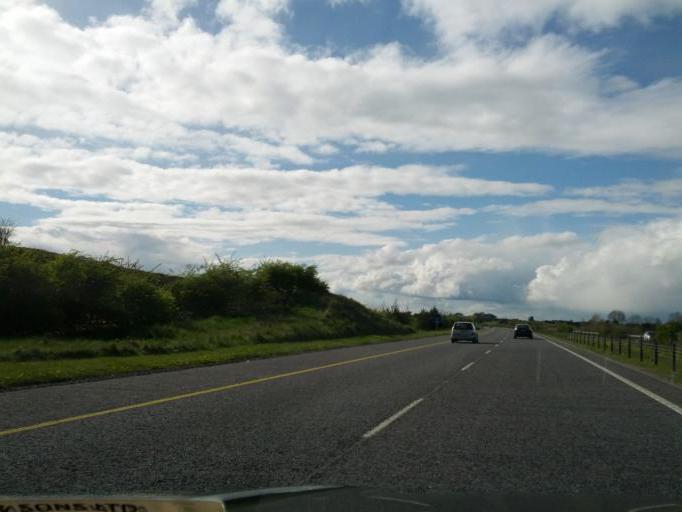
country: IE
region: Leinster
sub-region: An Mhi
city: Longwood
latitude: 53.4306
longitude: -6.9928
